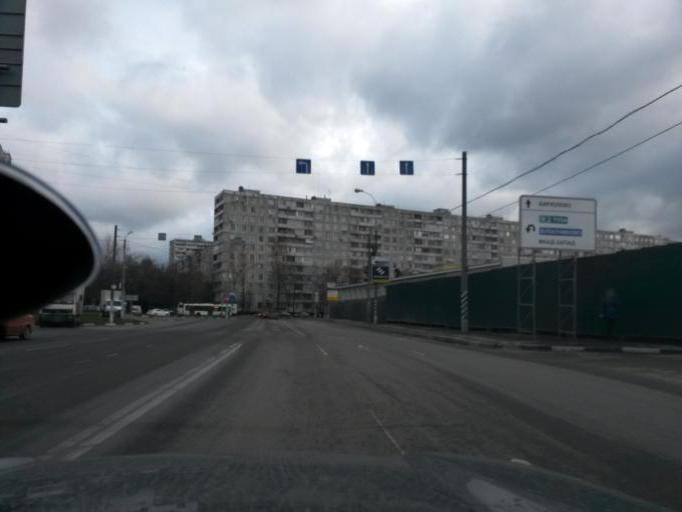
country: RU
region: Moscow
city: Zagor'ye
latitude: 55.5741
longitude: 37.6532
